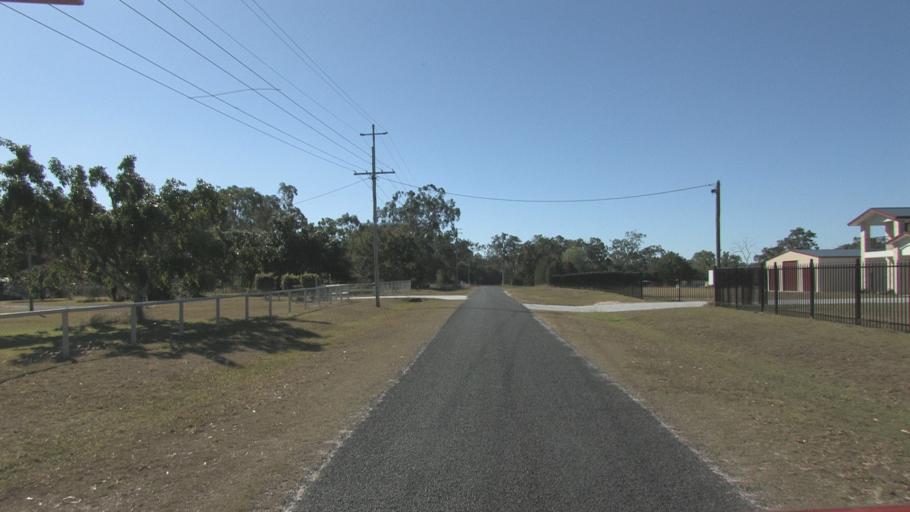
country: AU
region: Queensland
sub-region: Logan
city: Logan Reserve
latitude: -27.7312
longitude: 153.0781
